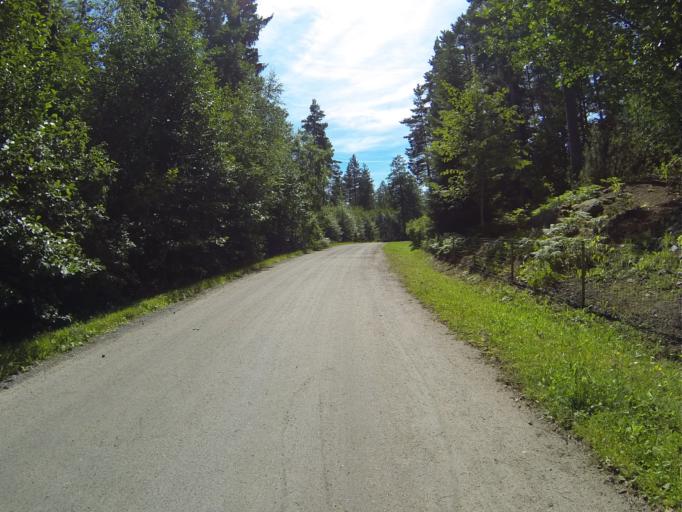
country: FI
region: Varsinais-Suomi
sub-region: Salo
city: Saerkisalo
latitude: 60.2574
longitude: 22.9708
